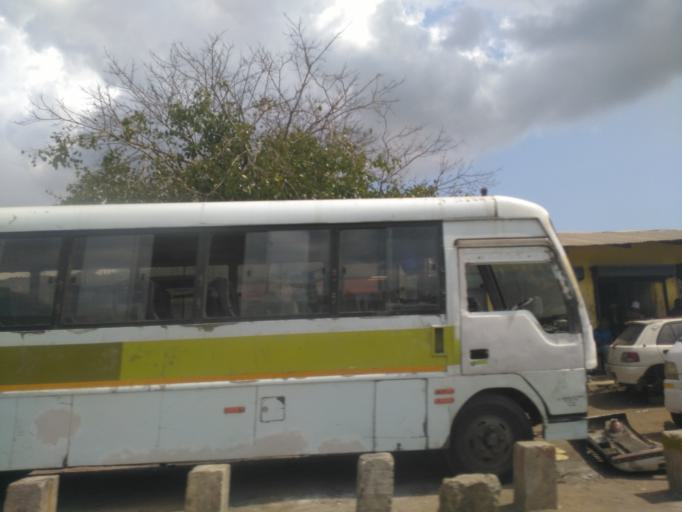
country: TZ
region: Dar es Salaam
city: Dar es Salaam
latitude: -6.8165
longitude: 39.2690
